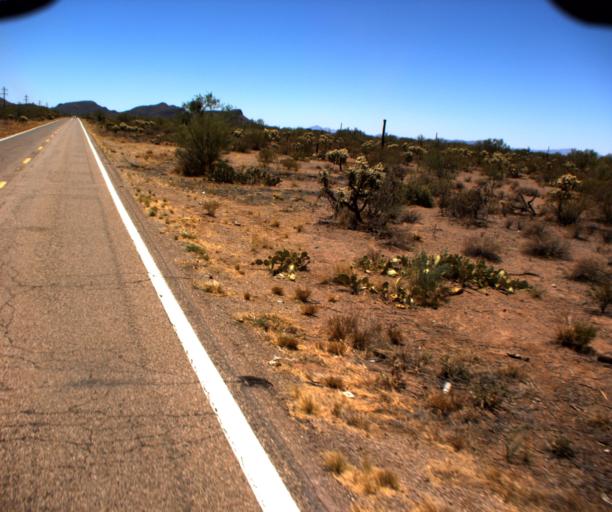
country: US
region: Arizona
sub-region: Pima County
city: Sells
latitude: 31.9979
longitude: -111.9836
